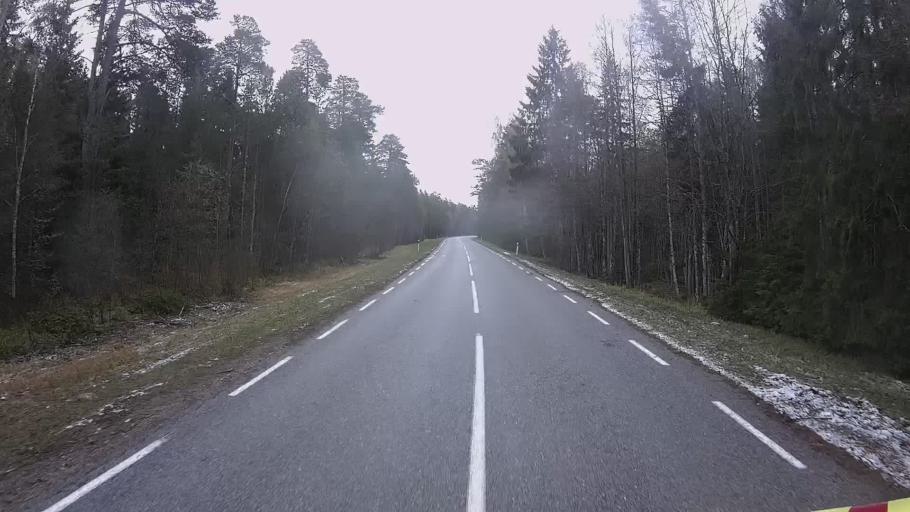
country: EE
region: Hiiumaa
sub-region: Kaerdla linn
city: Kardla
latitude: 59.0526
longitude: 22.6815
